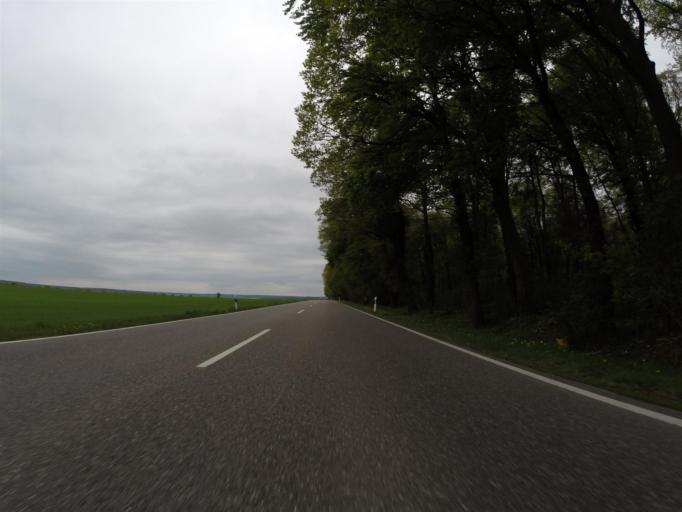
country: DE
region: Saxony-Anhalt
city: Naumburg
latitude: 51.1270
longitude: 11.7874
